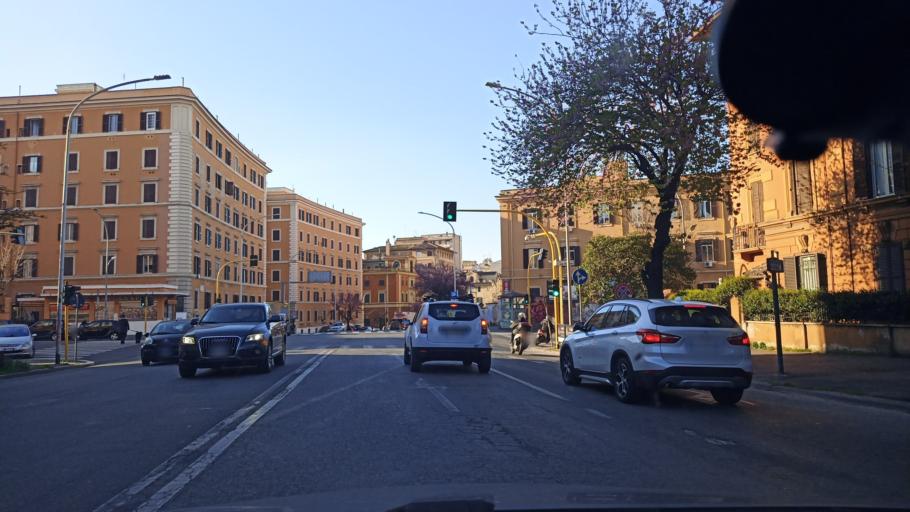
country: IT
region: Latium
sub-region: Citta metropolitana di Roma Capitale
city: Rome
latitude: 41.8868
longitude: 12.5152
